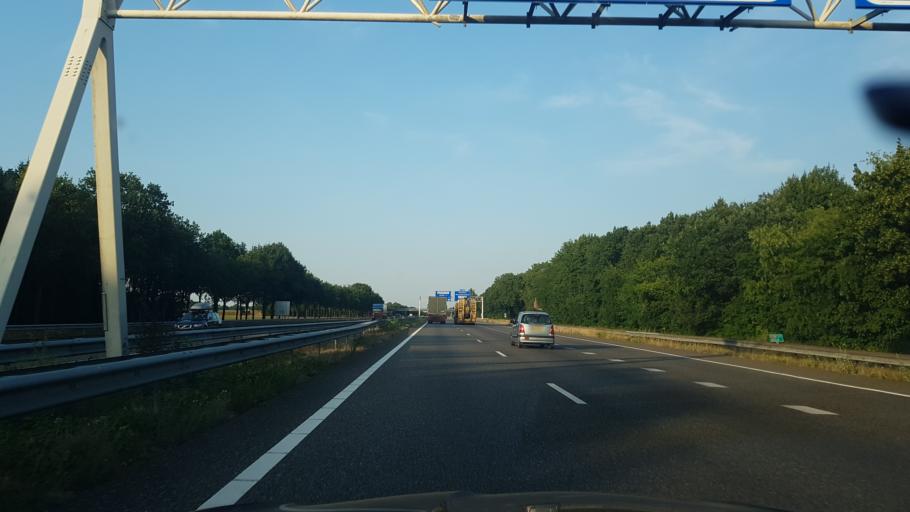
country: NL
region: North Brabant
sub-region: Gemeente Rucphen
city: Rucphen
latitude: 51.5499
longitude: 4.5379
